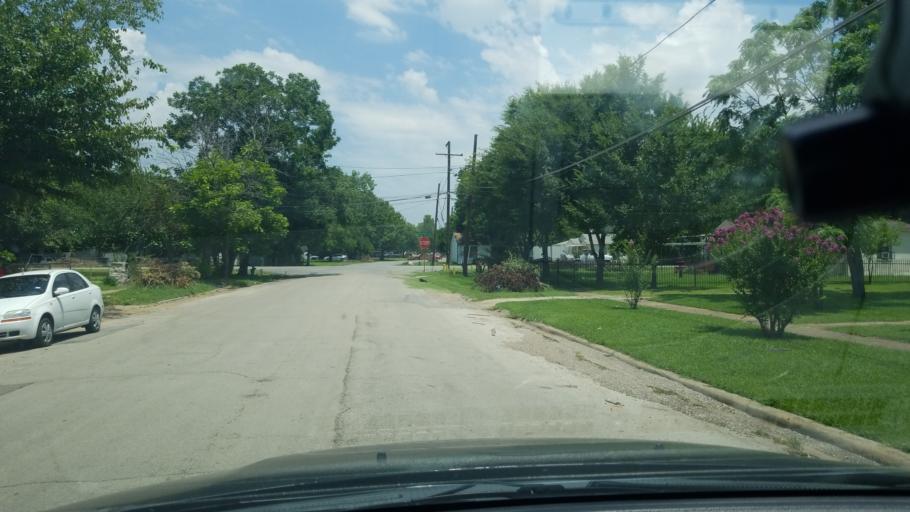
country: US
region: Texas
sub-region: Dallas County
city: Balch Springs
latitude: 32.7408
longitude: -96.6809
